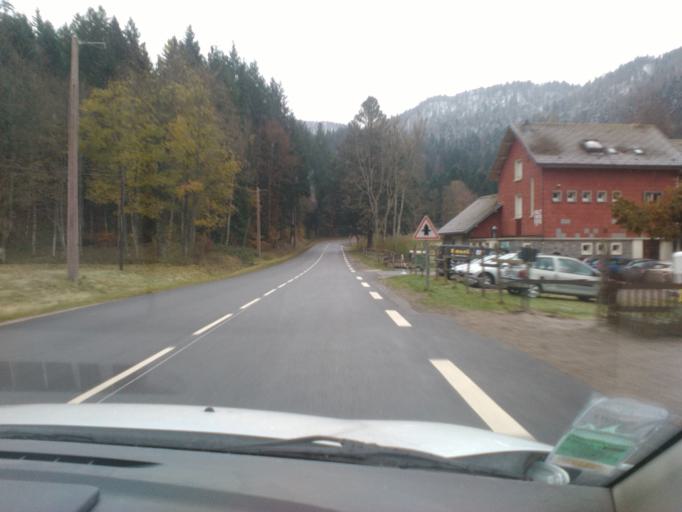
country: FR
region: Lorraine
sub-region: Departement des Vosges
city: Xonrupt-Longemer
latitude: 48.0575
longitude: 6.9861
